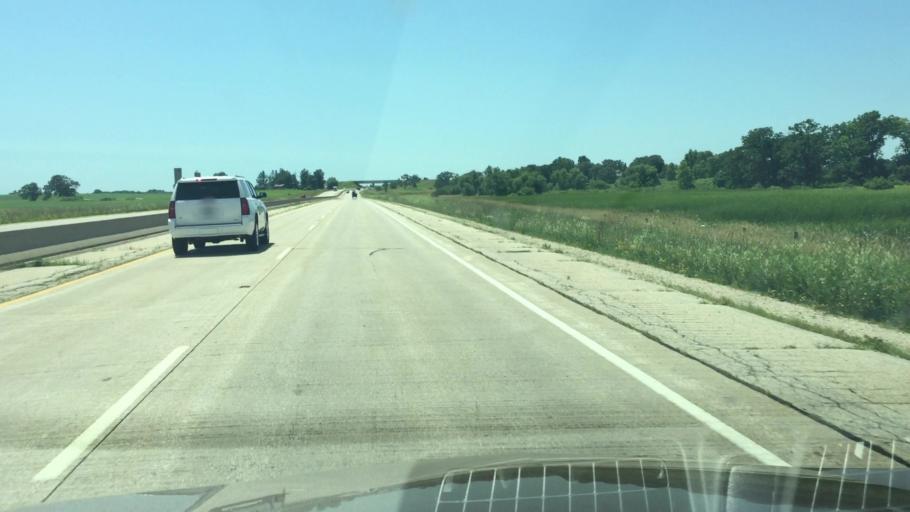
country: US
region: Wisconsin
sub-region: Fond du Lac County
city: Waupun
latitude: 43.5905
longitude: -88.7414
